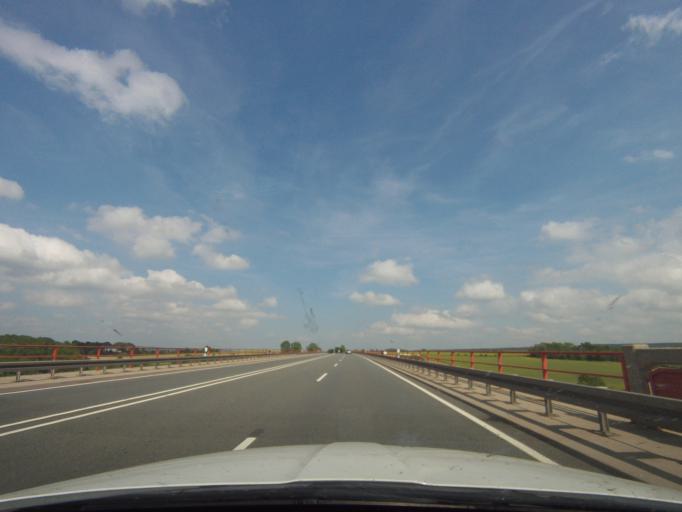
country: DE
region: Thuringia
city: Kospoda
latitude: 50.7240
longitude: 11.7416
